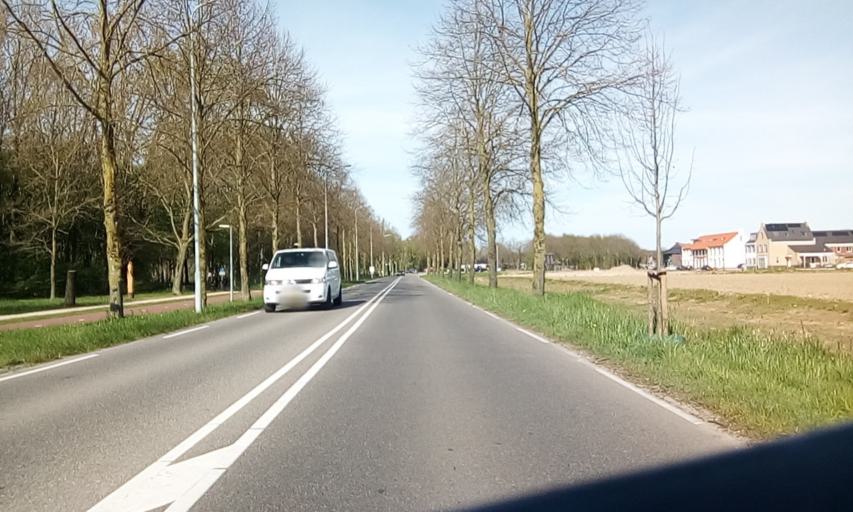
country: NL
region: Gelderland
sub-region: Gemeente Wijchen
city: Wijchen
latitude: 51.7978
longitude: 5.7361
